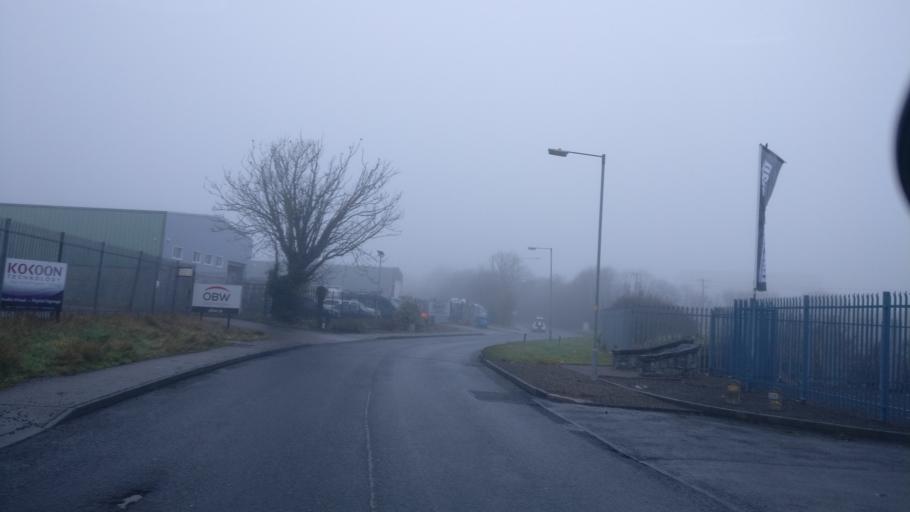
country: IE
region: Munster
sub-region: County Limerick
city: Luimneach
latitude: 52.6491
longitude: -8.5919
